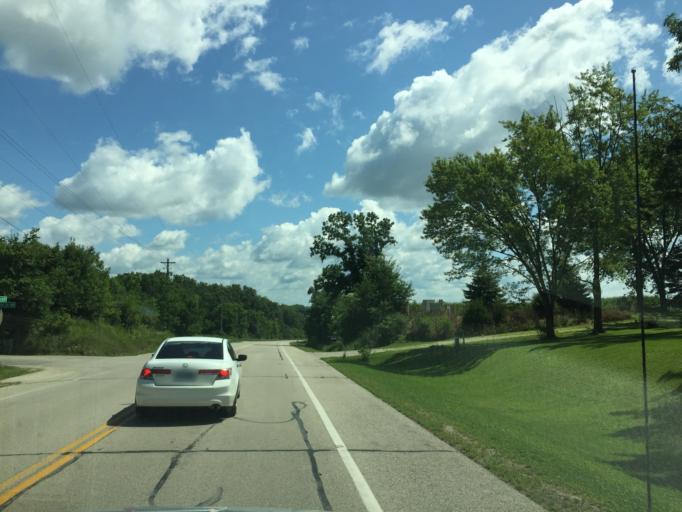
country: US
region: Minnesota
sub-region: Olmsted County
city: Rochester
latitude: 44.0237
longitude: -92.5471
